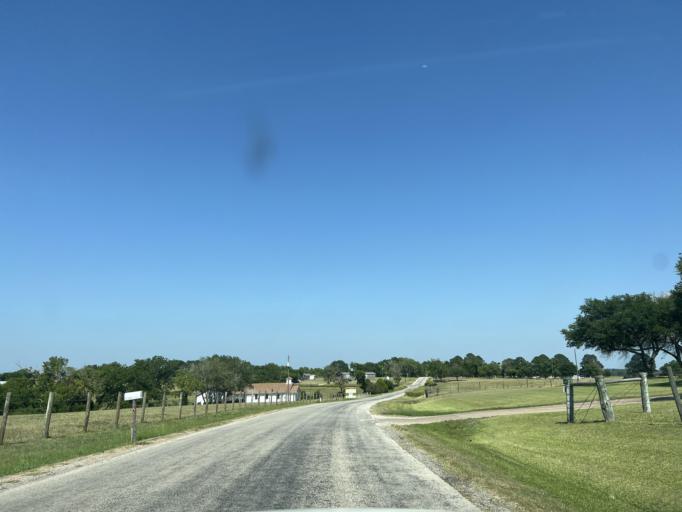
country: US
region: Texas
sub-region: Washington County
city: Brenham
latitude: 30.1722
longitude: -96.3678
